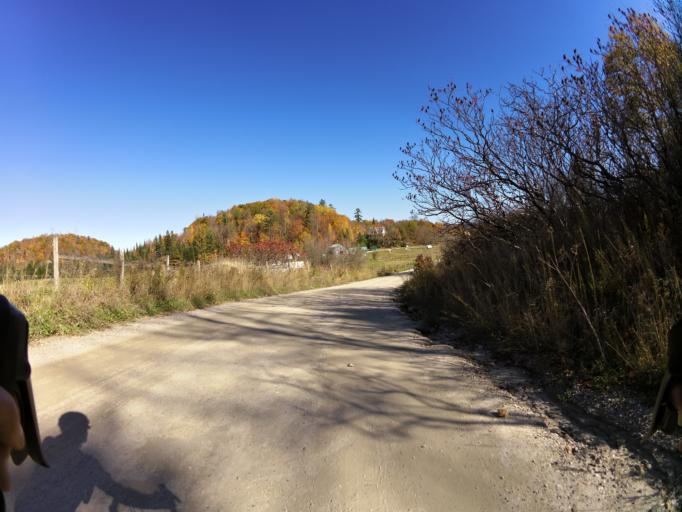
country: CA
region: Quebec
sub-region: Outaouais
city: Wakefield
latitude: 45.7758
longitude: -75.9689
